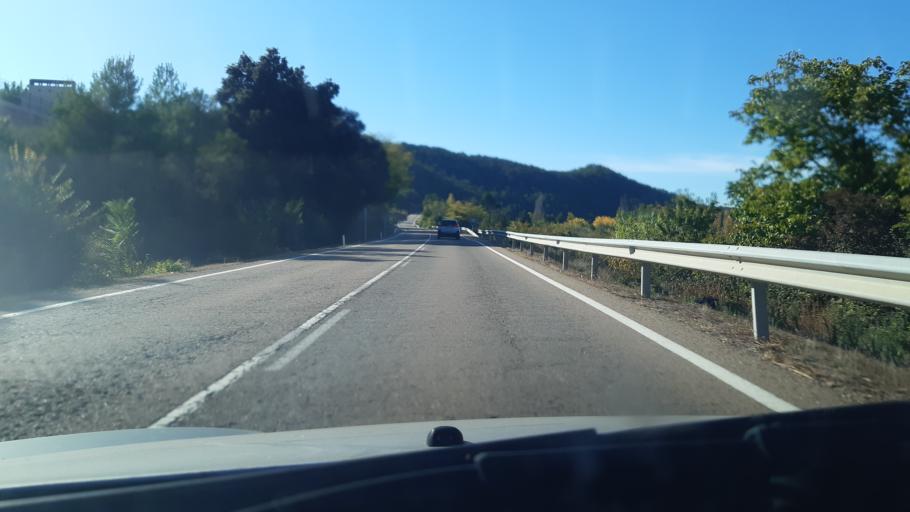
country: ES
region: Aragon
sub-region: Provincia de Teruel
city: Valderrobres
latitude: 40.8828
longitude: 0.1274
